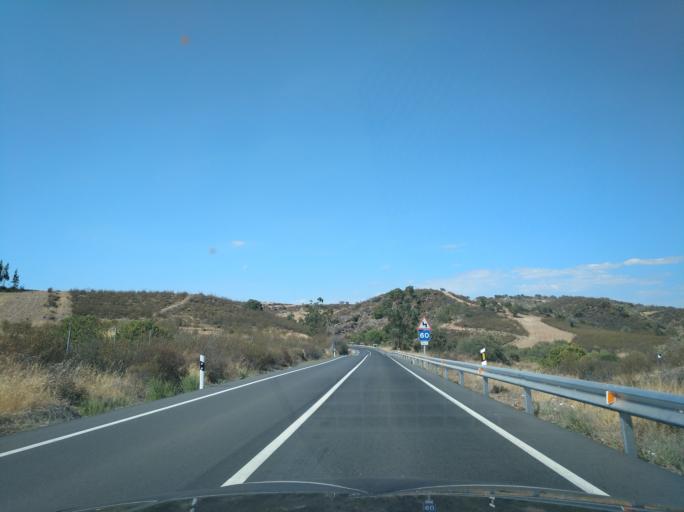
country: ES
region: Andalusia
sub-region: Provincia de Huelva
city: San Bartolome de la Torre
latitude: 37.4746
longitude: -7.1261
